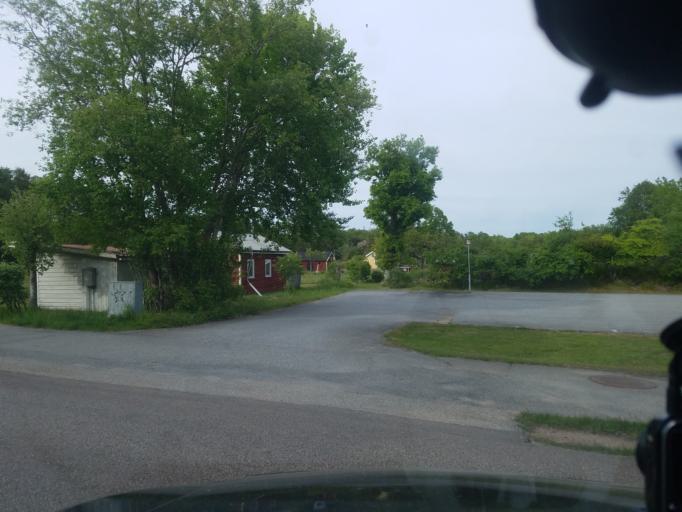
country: SE
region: Vaestra Goetaland
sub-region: Lysekils Kommun
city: Lysekil
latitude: 58.2893
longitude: 11.4576
